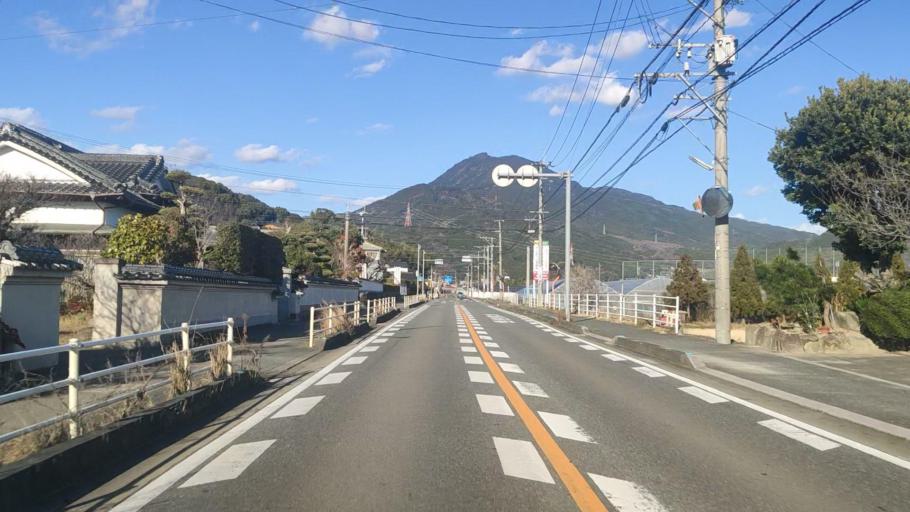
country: JP
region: Fukuoka
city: Dazaifu
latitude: 33.5010
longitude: 130.5496
